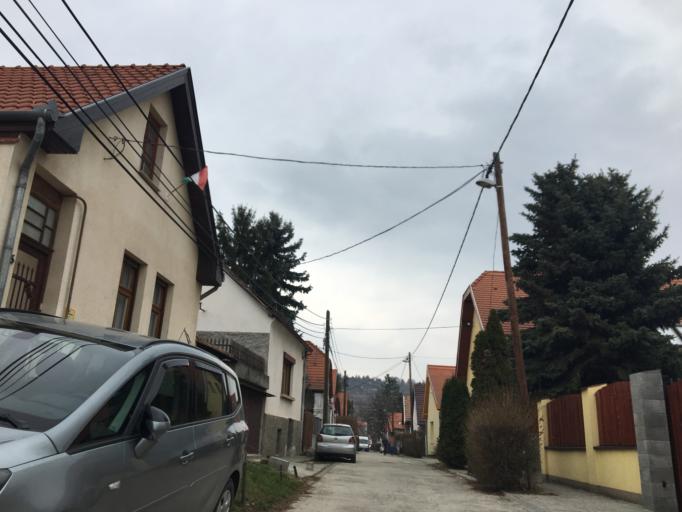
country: HU
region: Pest
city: Budakalasz
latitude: 47.6025
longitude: 19.0434
